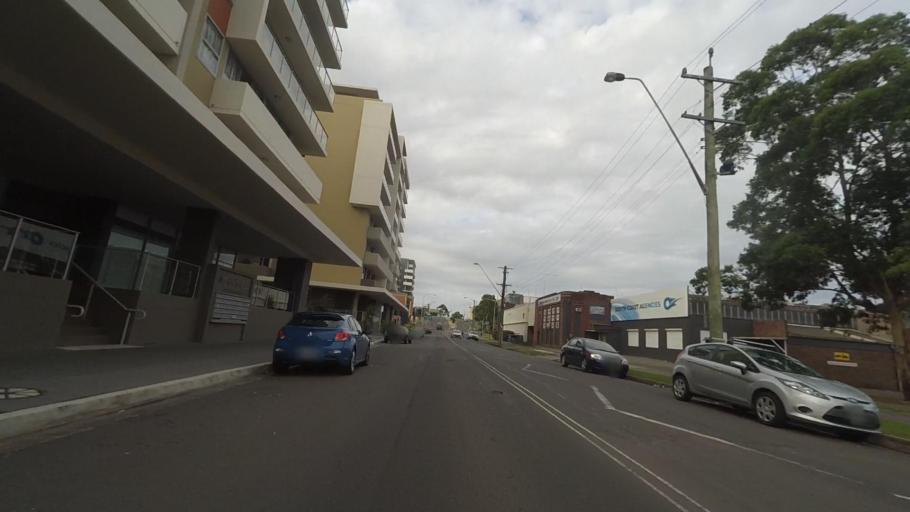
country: AU
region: New South Wales
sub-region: Wollongong
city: Wollongong
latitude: -34.4285
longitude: 150.8868
